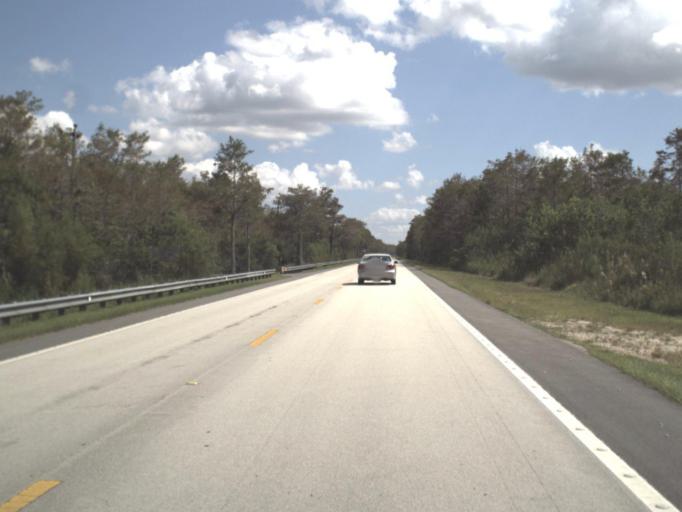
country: US
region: Florida
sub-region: Miami-Dade County
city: Kendall West
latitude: 25.8120
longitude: -80.8809
